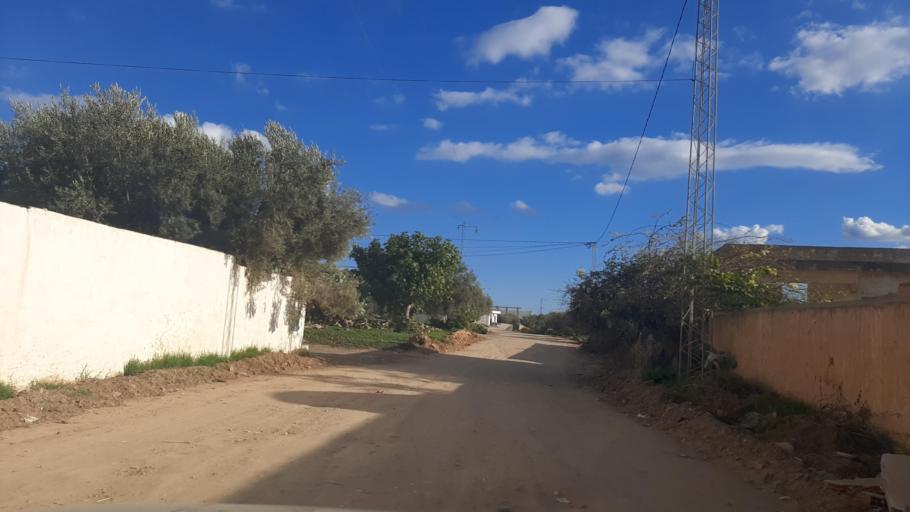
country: TN
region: Nabul
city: Al Hammamat
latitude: 36.4190
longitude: 10.5133
